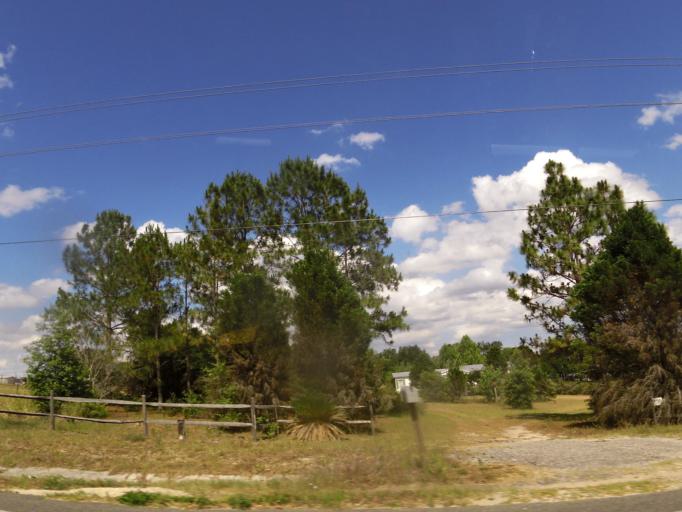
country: US
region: Florida
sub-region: Clay County
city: Keystone Heights
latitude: 29.8333
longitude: -81.9225
